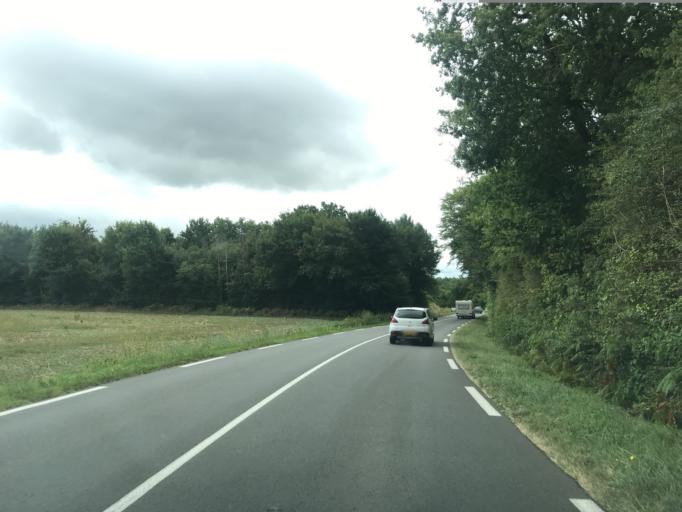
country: FR
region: Aquitaine
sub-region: Departement de la Dordogne
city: Mareuil
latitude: 45.4872
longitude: 0.3660
